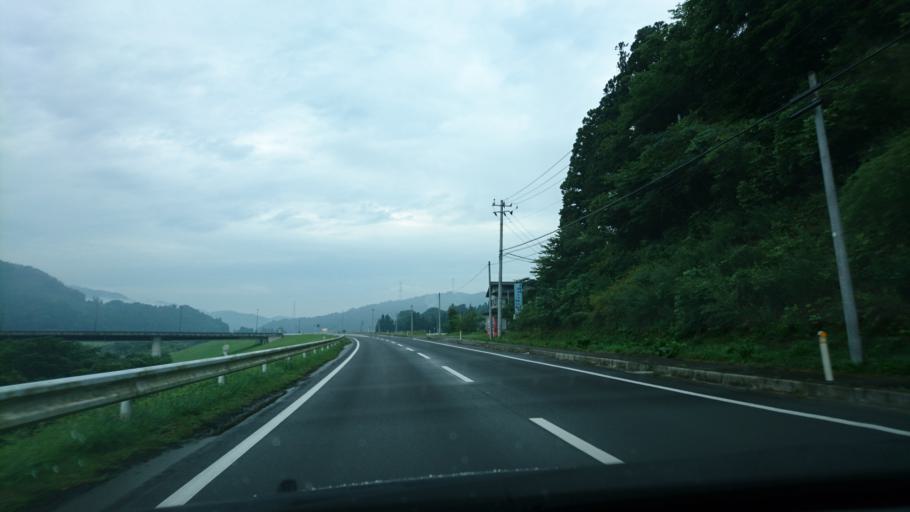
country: JP
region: Iwate
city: Ichinoseki
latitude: 38.9159
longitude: 141.2572
